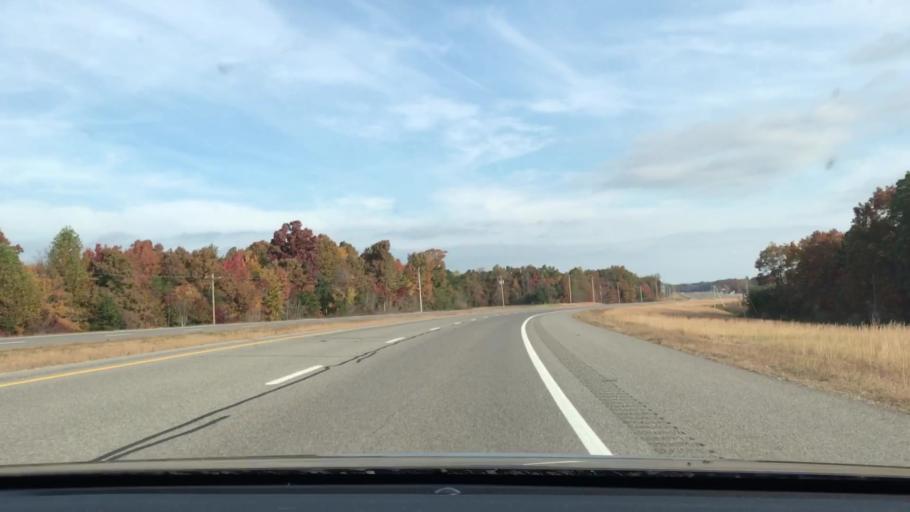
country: US
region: Tennessee
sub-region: Fentress County
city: Jamestown
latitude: 36.3493
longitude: -84.9523
